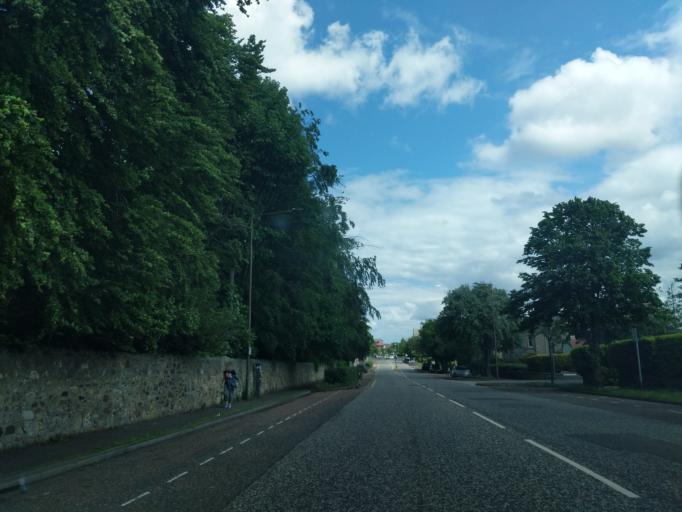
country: GB
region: Scotland
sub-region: Edinburgh
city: Edinburgh
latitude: 55.9577
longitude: -3.2311
